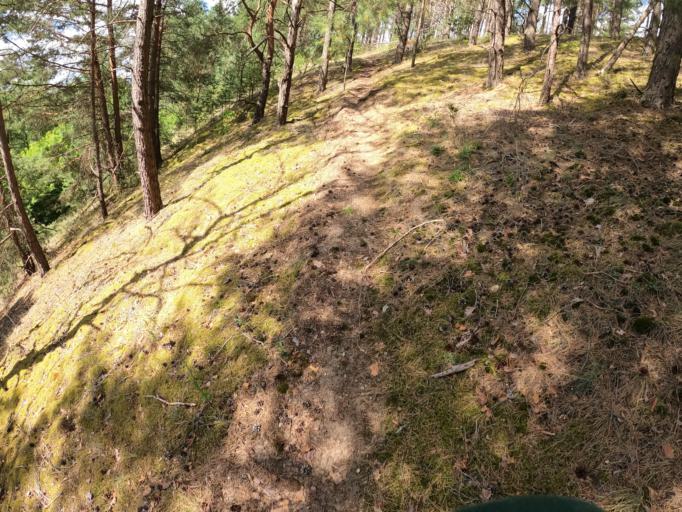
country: LT
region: Alytaus apskritis
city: Druskininkai
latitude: 54.1635
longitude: 24.1637
